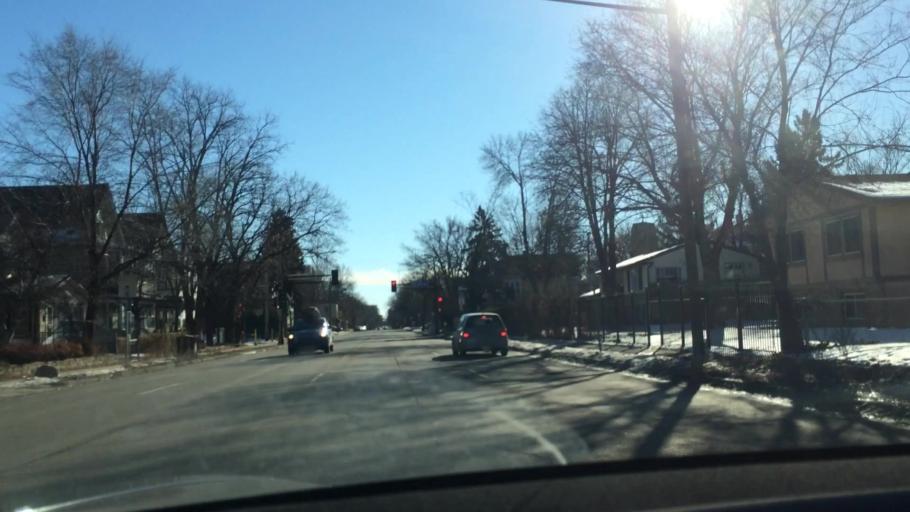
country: US
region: Minnesota
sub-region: Hennepin County
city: Minneapolis
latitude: 44.9973
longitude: -93.2628
